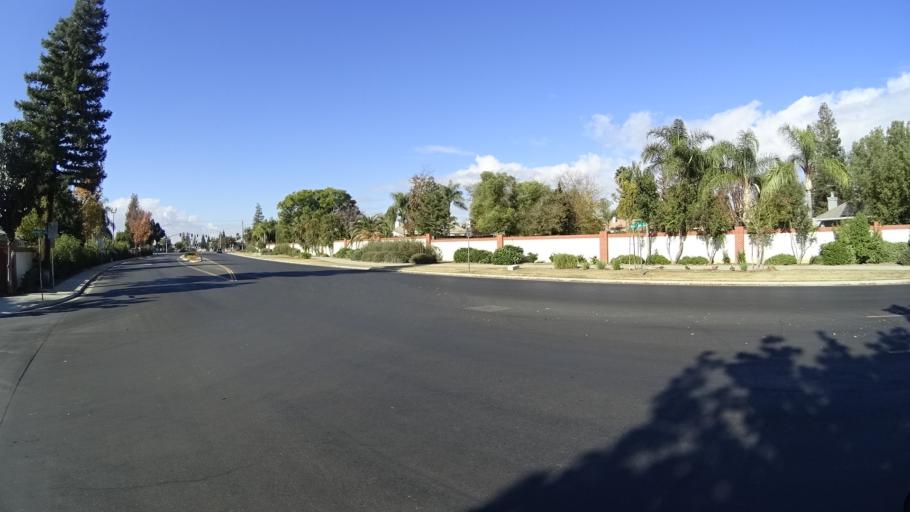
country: US
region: California
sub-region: Kern County
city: Greenacres
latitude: 35.3430
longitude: -119.1257
